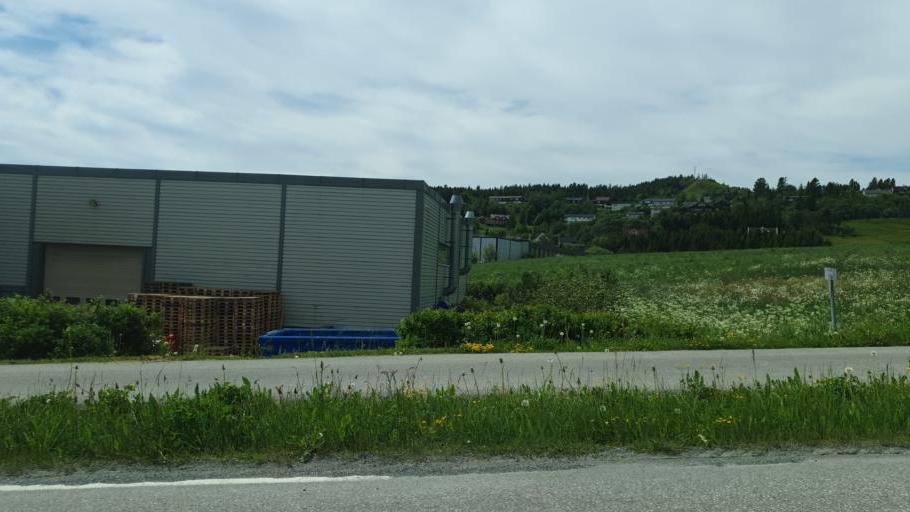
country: NO
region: Nord-Trondelag
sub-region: Leksvik
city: Leksvik
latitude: 63.6691
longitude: 10.6125
